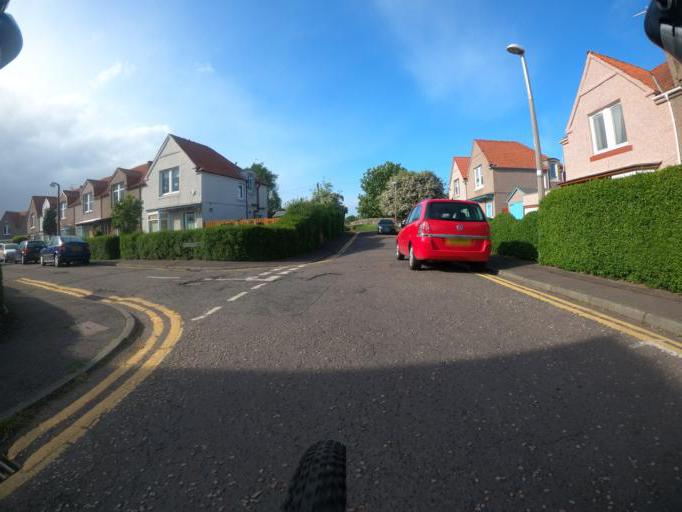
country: GB
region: Scotland
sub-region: Edinburgh
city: Edinburgh
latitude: 55.9729
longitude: -3.1999
